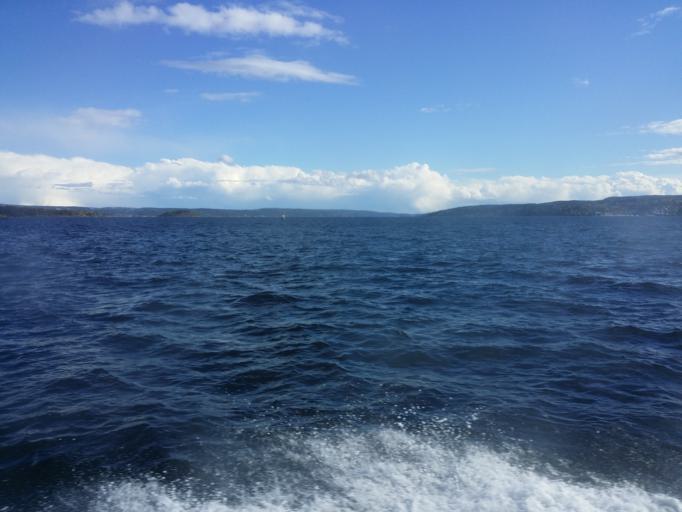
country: NO
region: Oslo
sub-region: Oslo
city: Sjolyststranda
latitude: 59.8930
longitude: 10.6822
